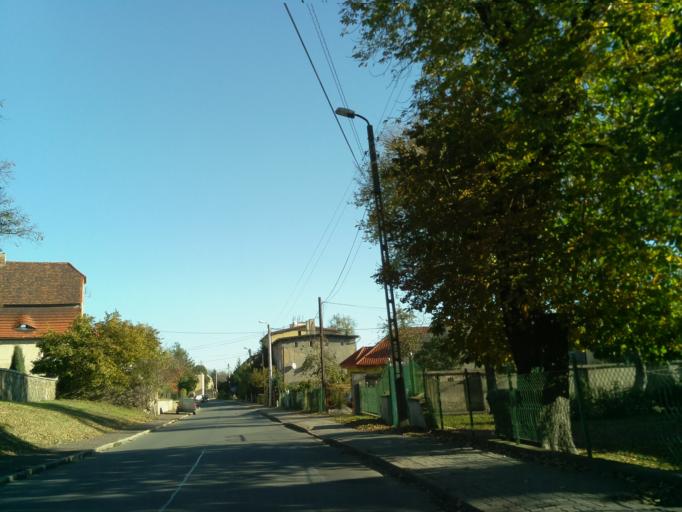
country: PL
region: Lower Silesian Voivodeship
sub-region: Powiat swidnicki
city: Swiebodzice
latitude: 50.8661
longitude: 16.3250
